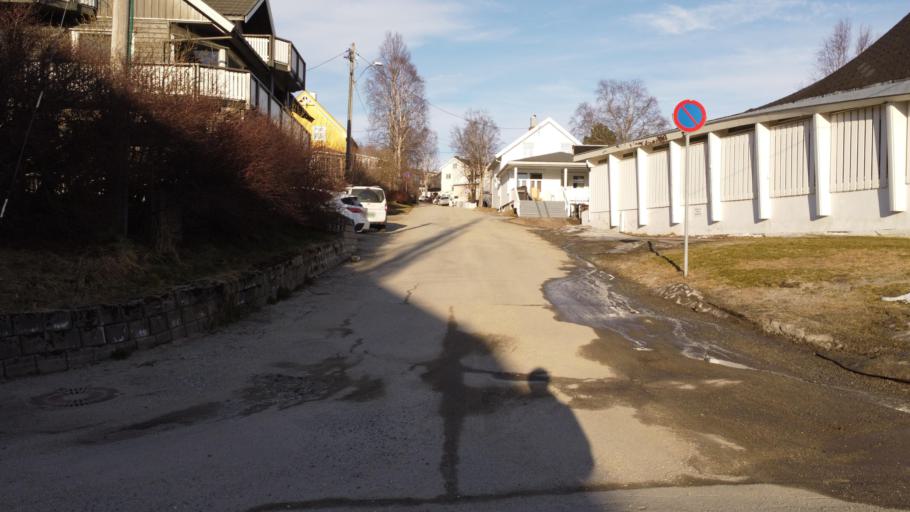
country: NO
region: Nordland
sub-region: Rana
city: Mo i Rana
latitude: 66.3135
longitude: 14.1336
